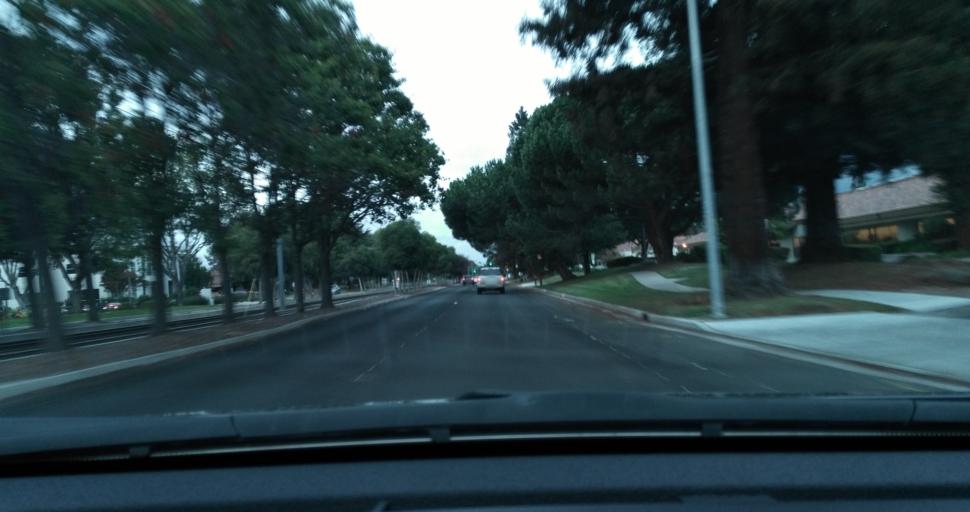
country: US
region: California
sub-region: Santa Clara County
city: Santa Clara
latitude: 37.3888
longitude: -121.9297
